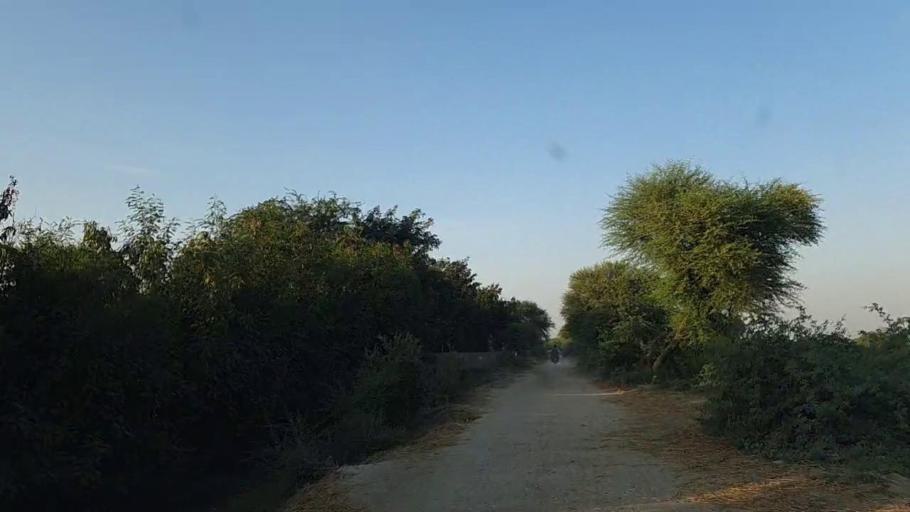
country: PK
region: Sindh
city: Mirpur Batoro
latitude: 24.7130
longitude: 68.2145
